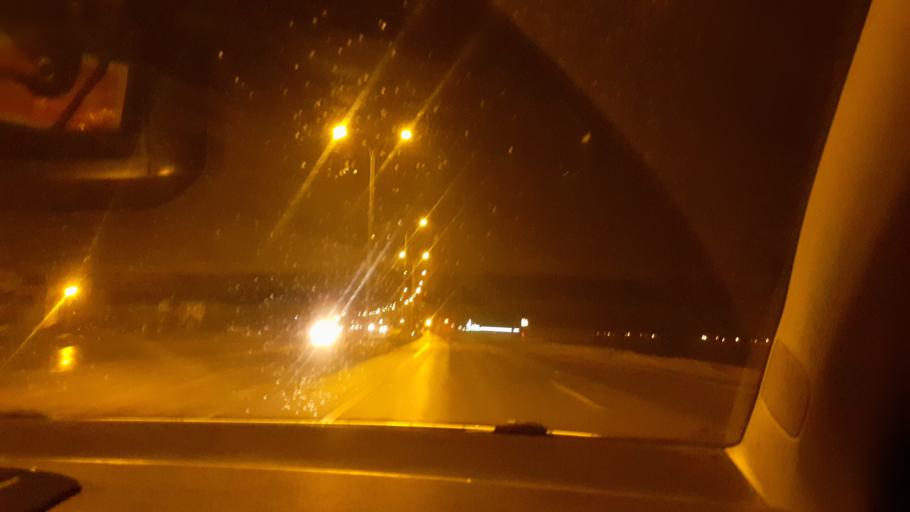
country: TR
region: Hatay
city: Aktepe
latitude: 36.7256
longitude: 36.5203
